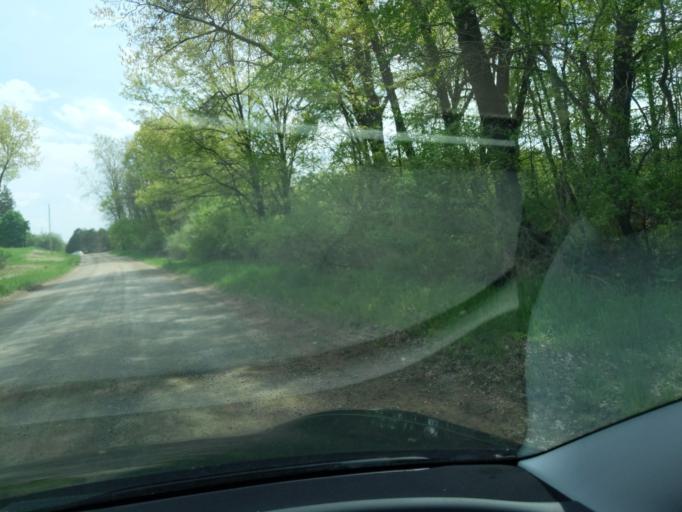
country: US
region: Michigan
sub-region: Ingham County
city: Stockbridge
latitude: 42.4338
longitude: -84.0762
